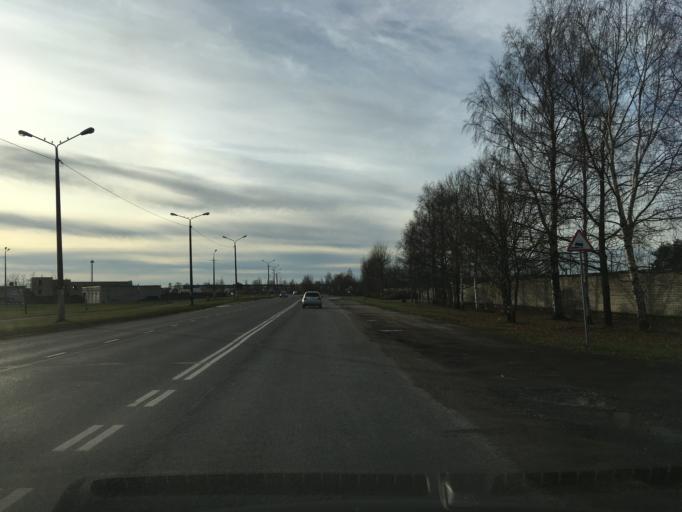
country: EE
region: Ida-Virumaa
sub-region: Narva linn
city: Narva
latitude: 59.3802
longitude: 28.1564
